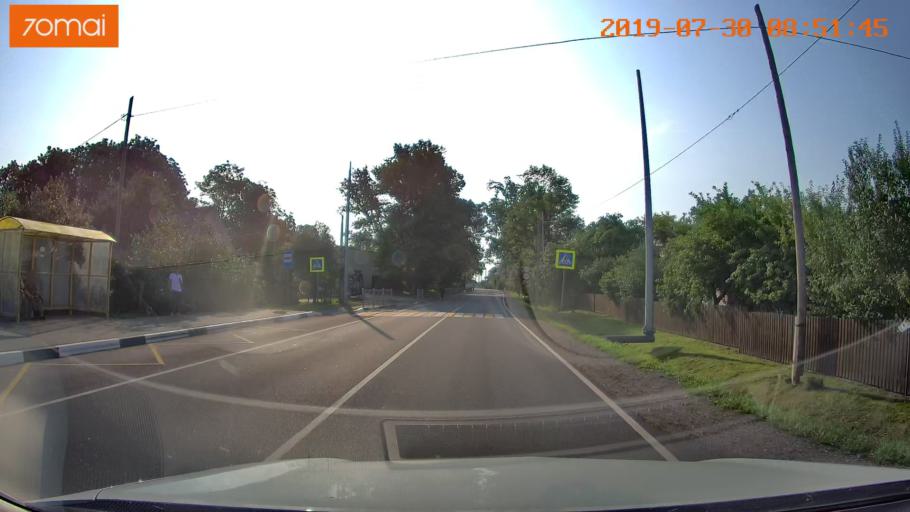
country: RU
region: Kaliningrad
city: Chernyakhovsk
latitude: 54.6011
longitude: 21.9646
